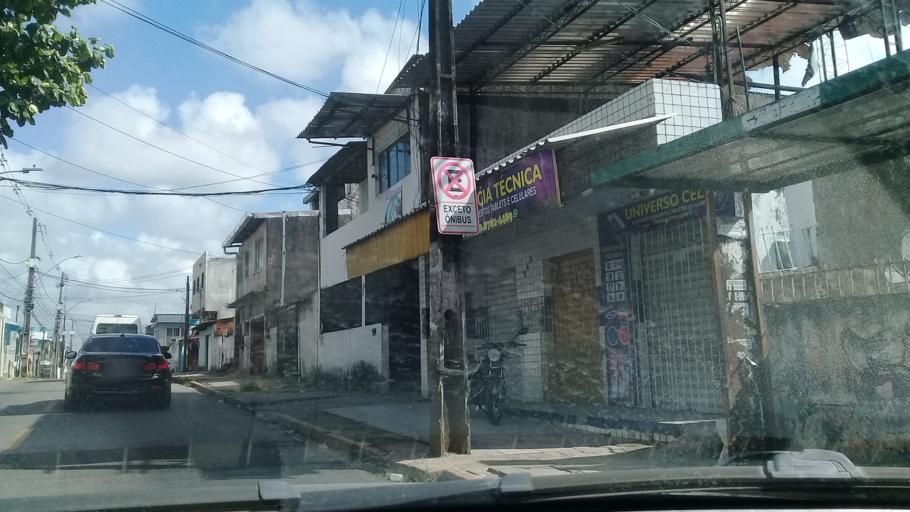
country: BR
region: Pernambuco
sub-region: Jaboatao Dos Guararapes
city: Jaboatao dos Guararapes
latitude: -8.1177
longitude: -34.9466
